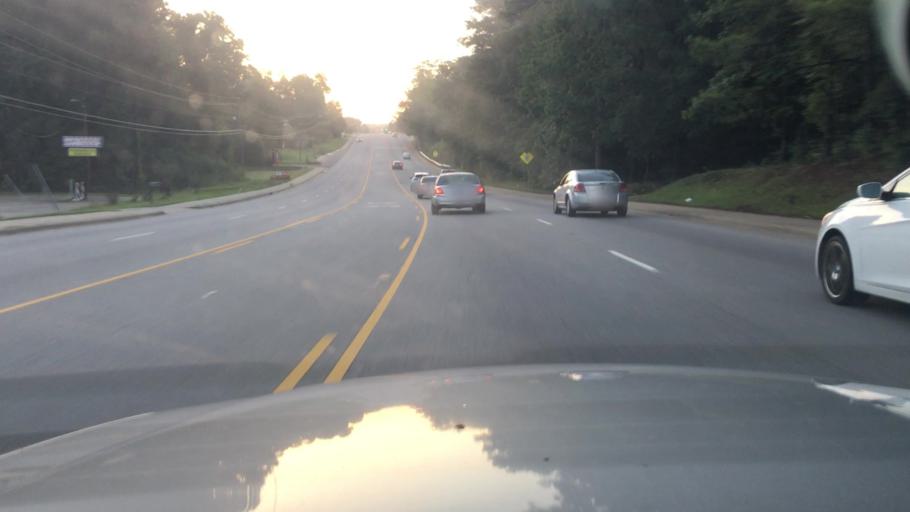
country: US
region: North Carolina
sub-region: Cumberland County
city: Fort Bragg
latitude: 35.0578
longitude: -79.0003
